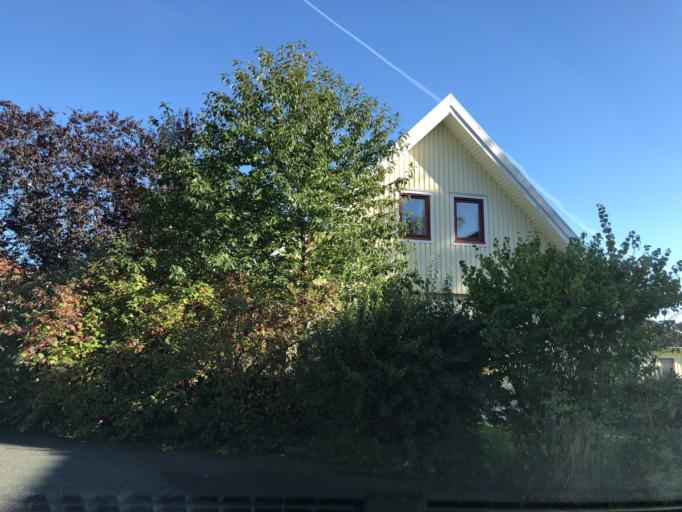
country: SE
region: Vaestra Goetaland
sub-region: Goteborg
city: Majorna
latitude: 57.6532
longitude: 11.8612
